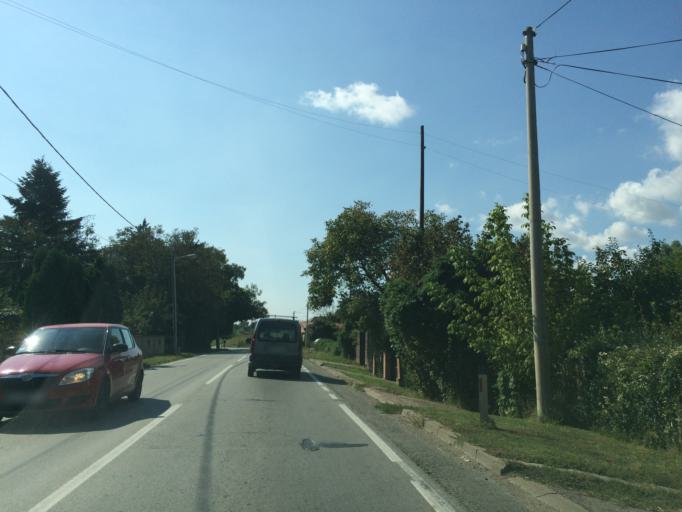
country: RS
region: Autonomna Pokrajina Vojvodina
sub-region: Juznobacki Okrug
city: Novi Sad
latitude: 45.2203
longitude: 19.8277
